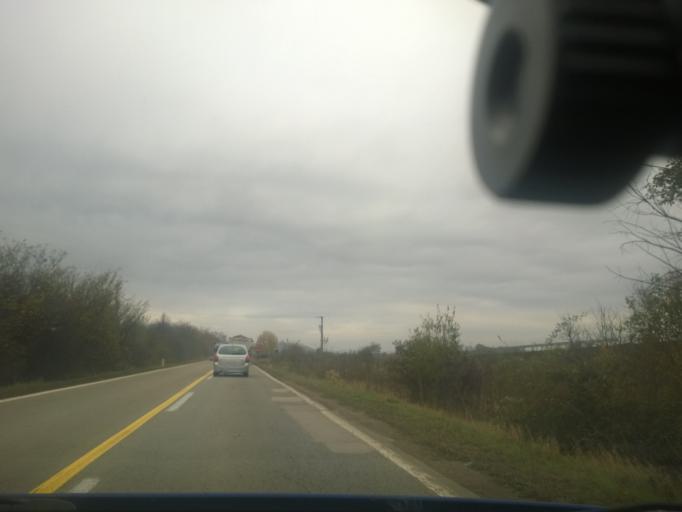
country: RS
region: Central Serbia
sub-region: Pirotski Okrug
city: Dimitrovgrad
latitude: 43.0579
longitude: 22.6899
